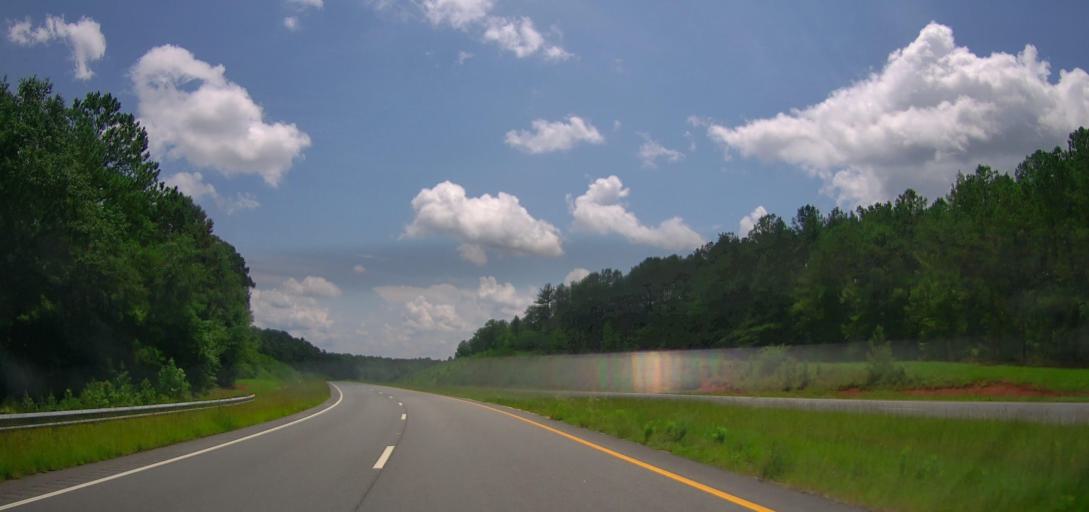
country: US
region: Georgia
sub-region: Upson County
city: Thomaston
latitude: 32.8418
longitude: -84.3133
